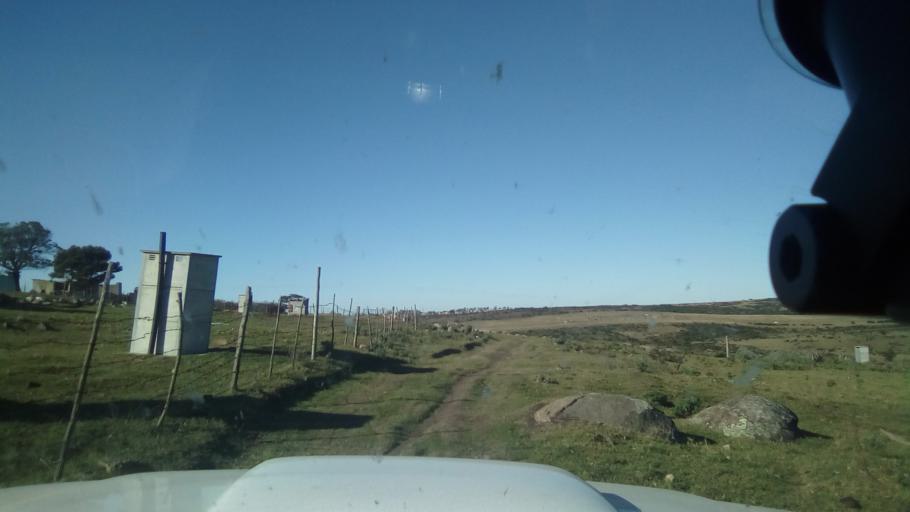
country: ZA
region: Eastern Cape
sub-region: Buffalo City Metropolitan Municipality
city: Bhisho
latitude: -32.9400
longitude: 27.2907
